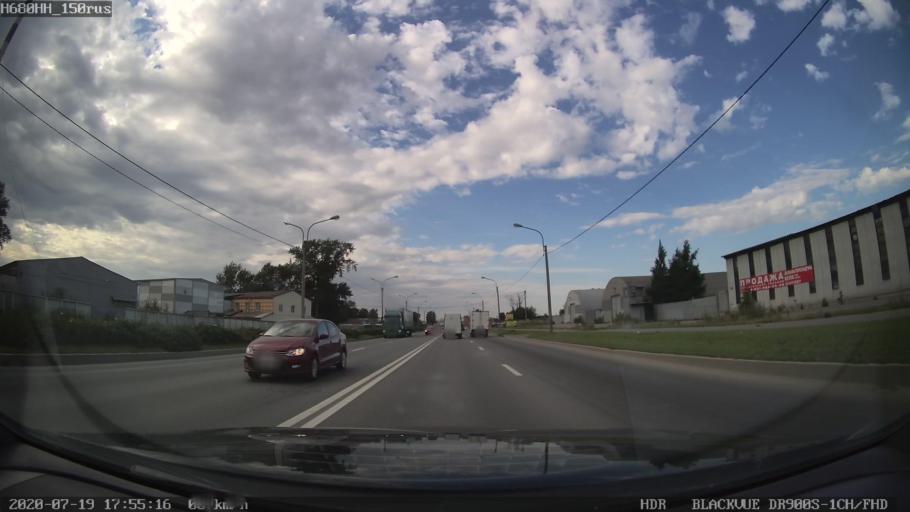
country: RU
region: St.-Petersburg
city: Admiralteisky
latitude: 59.8934
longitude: 30.3012
